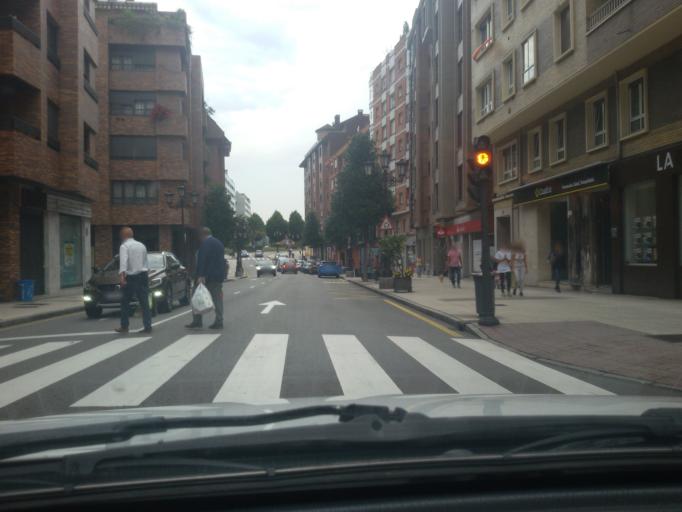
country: ES
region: Asturias
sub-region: Province of Asturias
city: Oviedo
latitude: 43.3684
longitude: -5.8494
